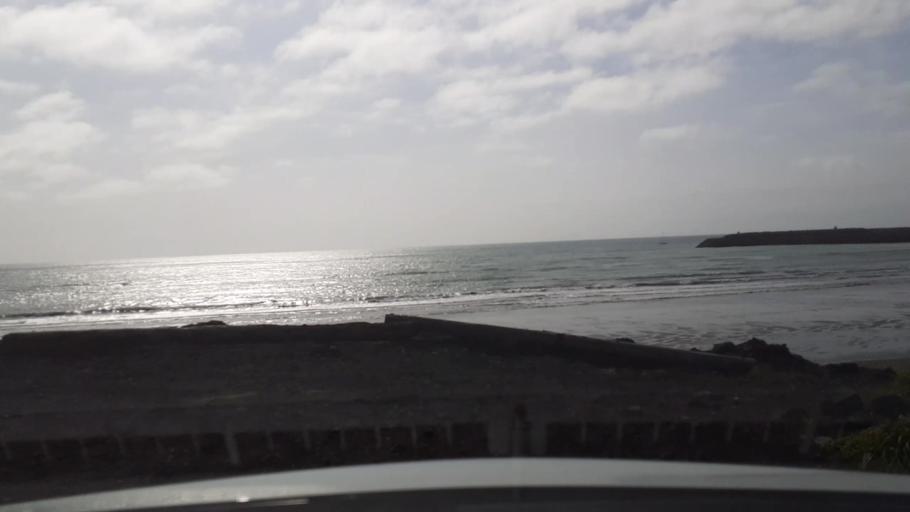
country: IS
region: South
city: THorlakshoefn
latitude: 63.8693
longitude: -21.3730
